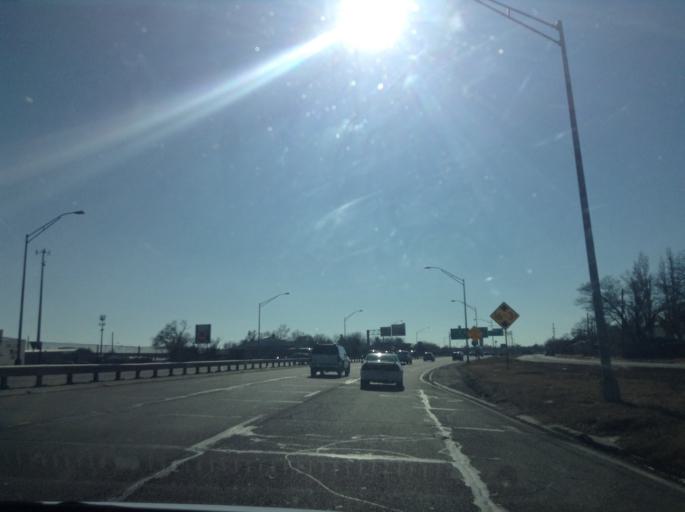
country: US
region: Texas
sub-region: Potter County
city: Amarillo
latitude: 35.1828
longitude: -101.8386
